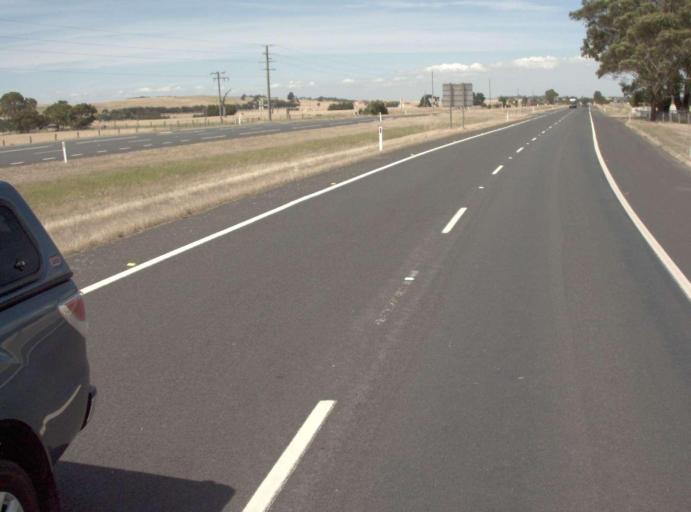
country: AU
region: Victoria
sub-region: Wellington
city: Heyfield
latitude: -38.1369
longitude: 146.7965
